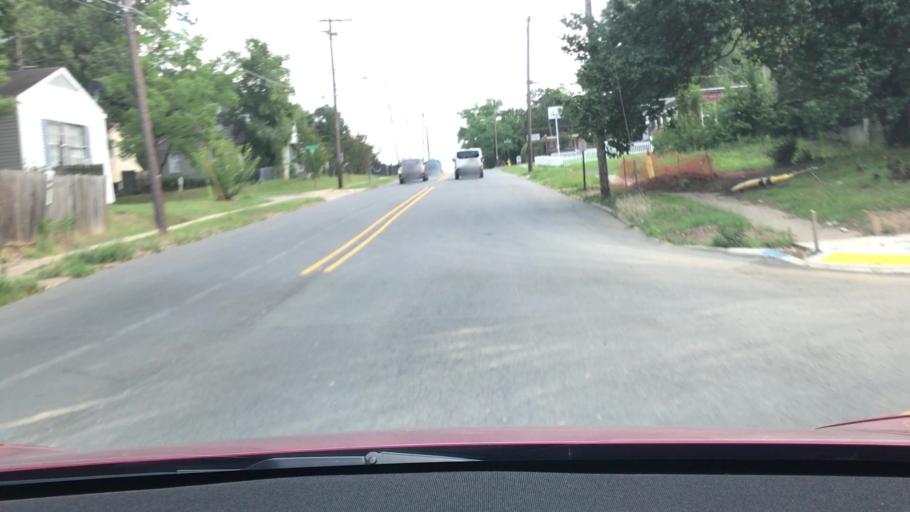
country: US
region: Louisiana
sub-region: Bossier Parish
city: Bossier City
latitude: 32.4954
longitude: -93.7333
